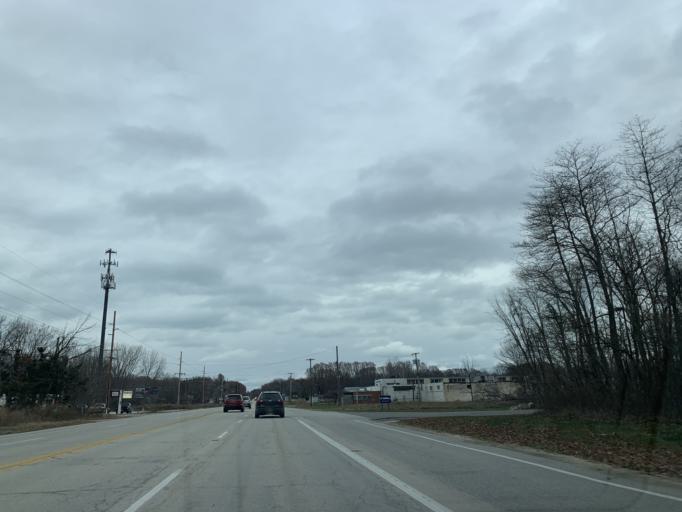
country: US
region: Indiana
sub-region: LaPorte County
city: Long Beach
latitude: 41.7340
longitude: -86.8261
